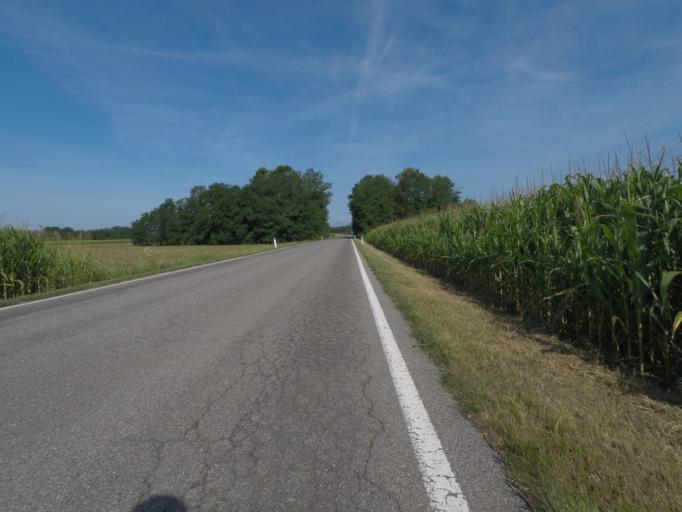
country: IT
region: Friuli Venezia Giulia
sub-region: Provincia di Udine
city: Colloredo di Prato
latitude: 46.0551
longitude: 13.1214
